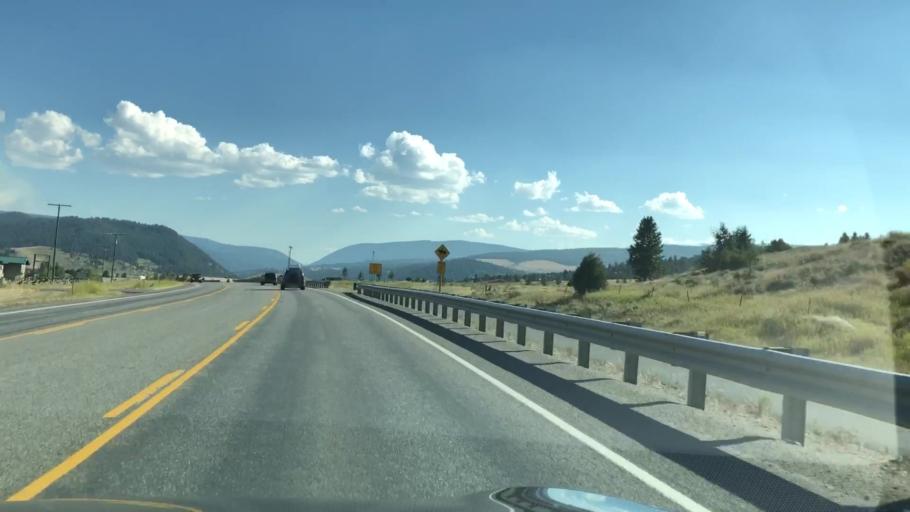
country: US
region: Montana
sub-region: Gallatin County
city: Big Sky
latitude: 45.2538
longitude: -111.2552
